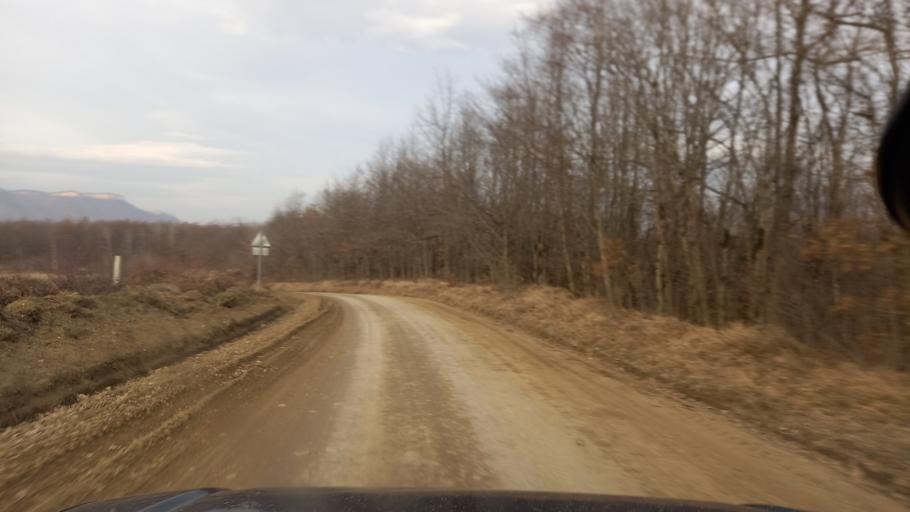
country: RU
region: Adygeya
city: Kamennomostskiy
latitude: 44.1589
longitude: 40.2441
